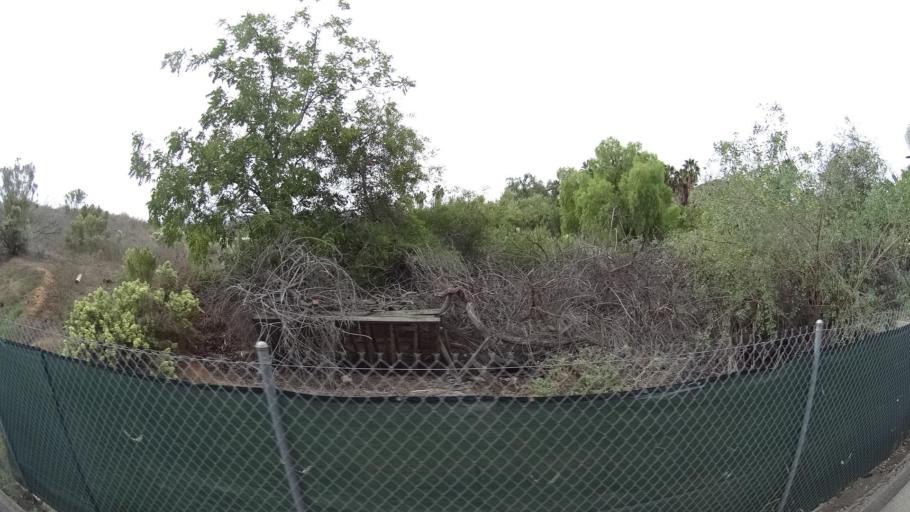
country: US
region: California
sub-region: San Diego County
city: Rancho San Diego
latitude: 32.7639
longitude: -116.9254
